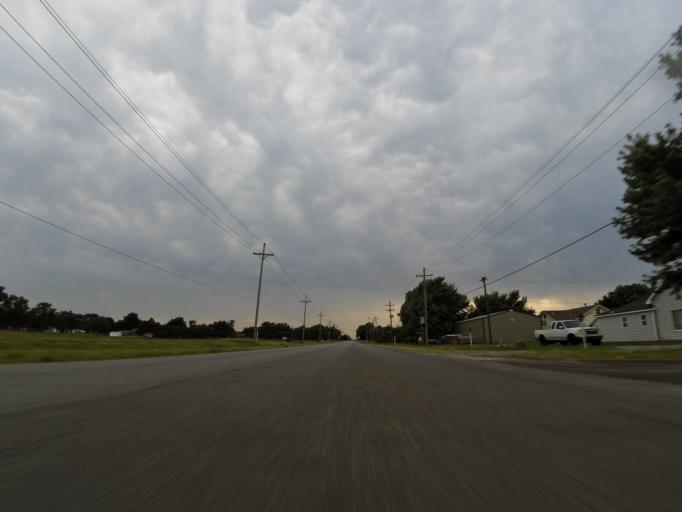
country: US
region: Kansas
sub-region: Reno County
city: South Hutchinson
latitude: 38.0284
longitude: -97.9558
